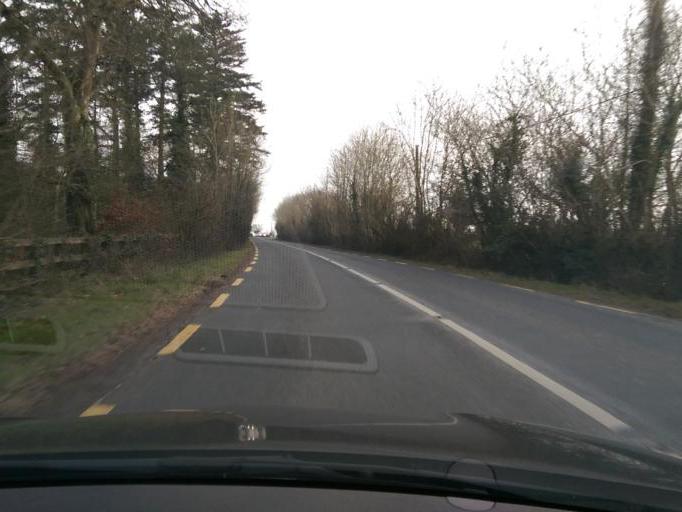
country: IE
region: Leinster
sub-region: An Iarmhi
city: Athlone
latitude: 53.4593
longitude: -7.8777
